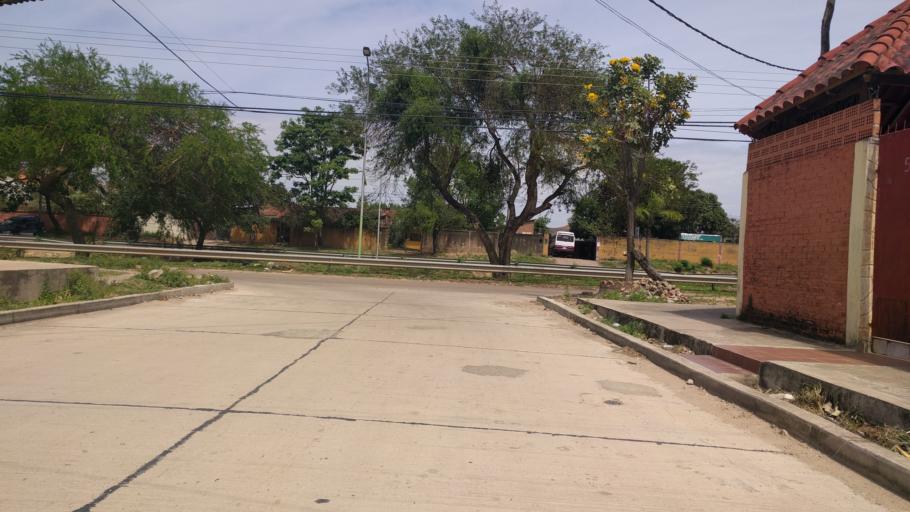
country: BO
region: Santa Cruz
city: Santa Cruz de la Sierra
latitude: -17.8185
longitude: -63.2237
